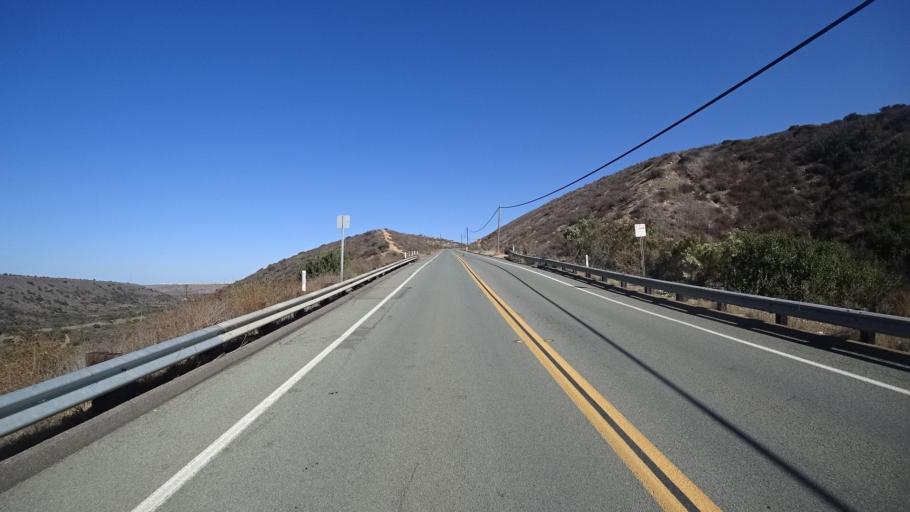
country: MX
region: Baja California
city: Tijuana
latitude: 32.5882
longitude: -116.9269
